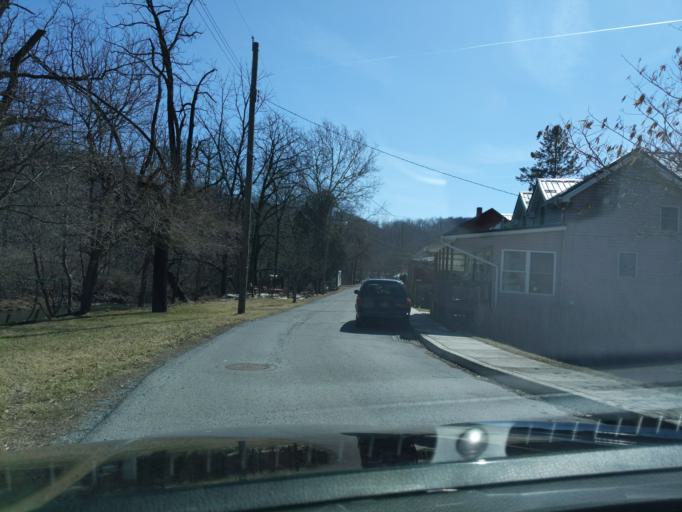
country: US
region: Pennsylvania
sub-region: Blair County
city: Hollidaysburg
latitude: 40.4240
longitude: -78.3936
